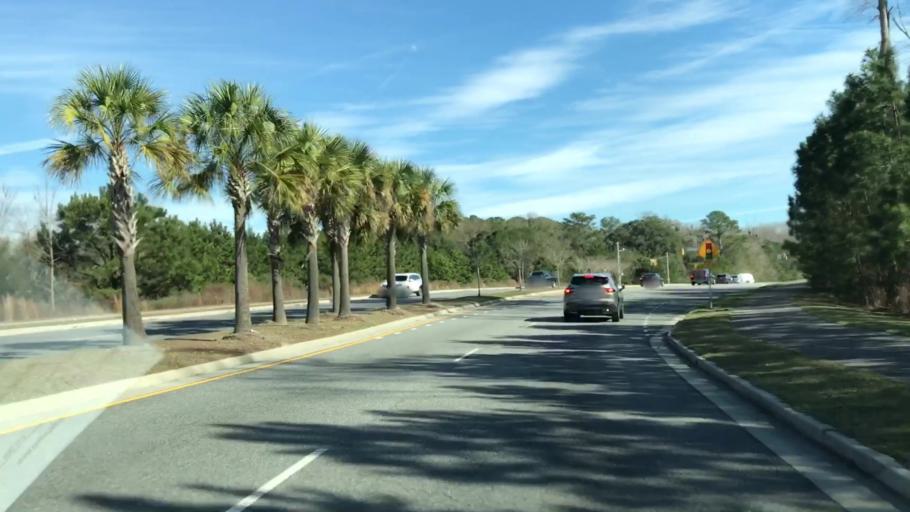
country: US
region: South Carolina
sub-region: Beaufort County
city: Bluffton
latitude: 32.2649
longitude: -80.8833
